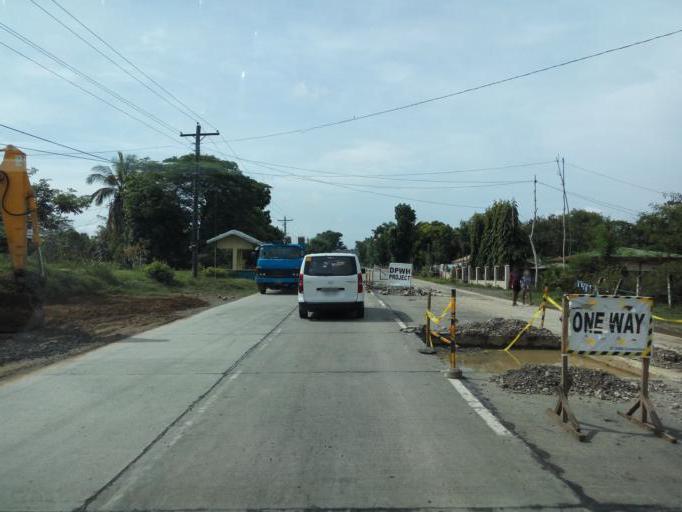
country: PH
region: Cagayan Valley
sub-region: Province of Isabela
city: Gamu
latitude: 17.0533
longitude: 121.8568
